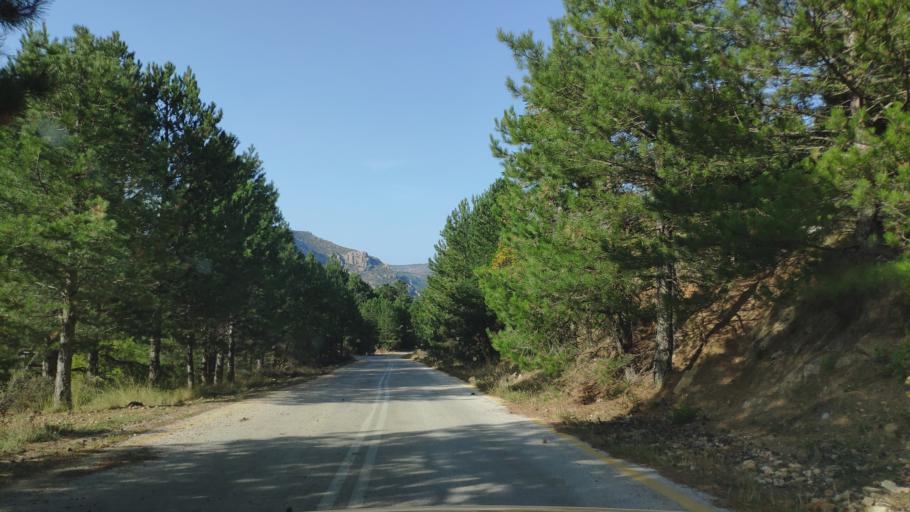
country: GR
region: West Greece
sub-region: Nomos Achaias
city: Aiyira
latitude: 38.0555
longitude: 22.3818
